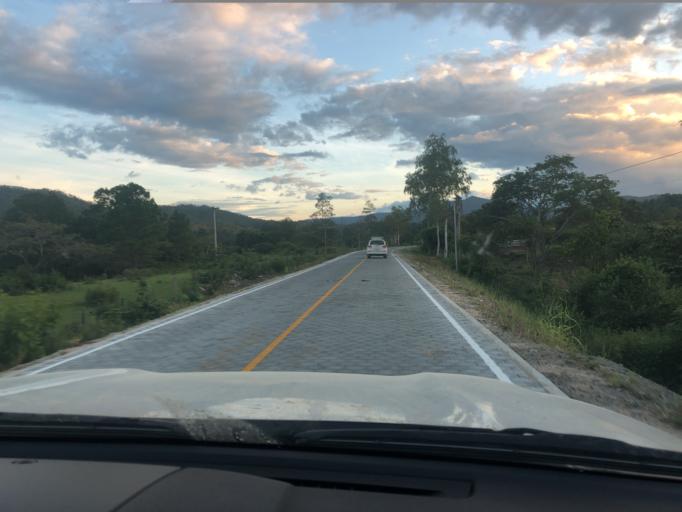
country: HN
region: El Paraiso
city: Santa Cruz
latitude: 13.7213
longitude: -86.6226
